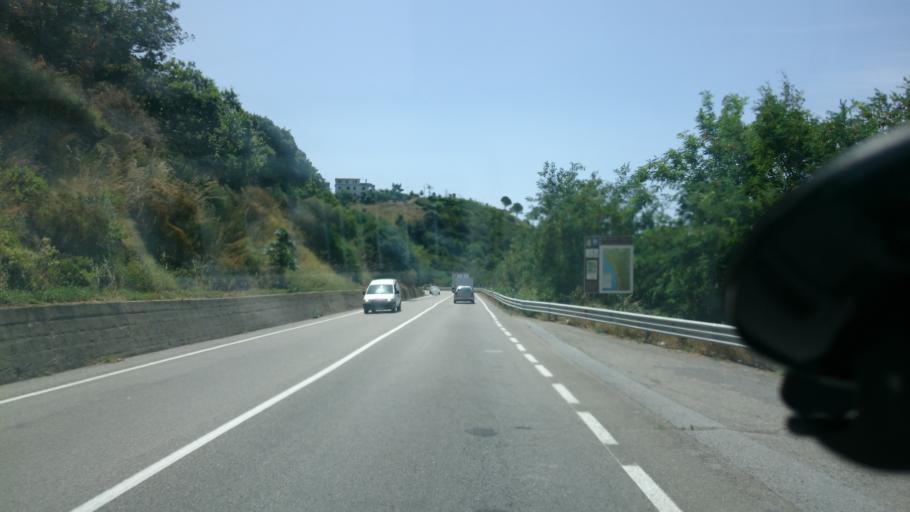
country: IT
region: Calabria
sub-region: Provincia di Cosenza
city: Cittadella del Capo
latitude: 39.5488
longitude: 15.8821
